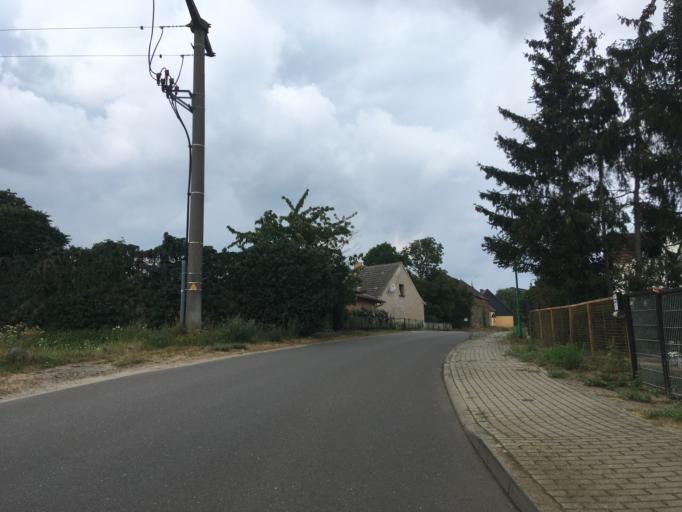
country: DE
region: Brandenburg
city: Angermunde
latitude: 52.9793
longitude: 13.9620
